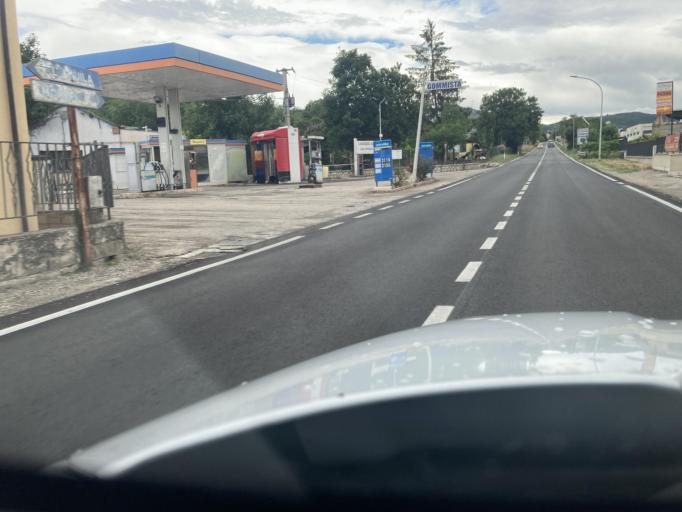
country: IT
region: Abruzzo
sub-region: Provincia dell' Aquila
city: Sant'Eusanio Forconese
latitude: 42.2949
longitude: 13.5370
